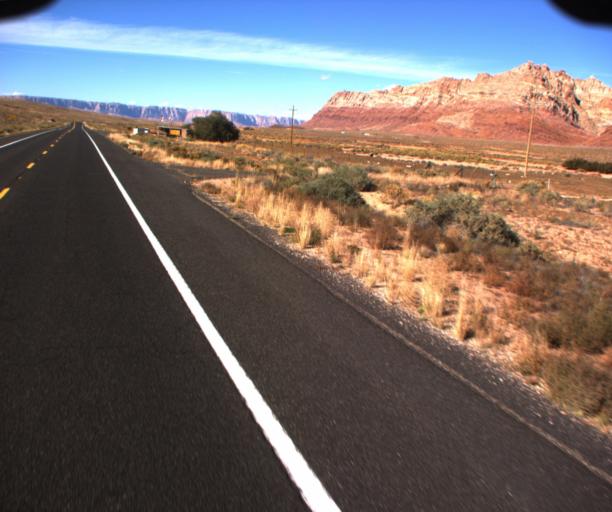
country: US
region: Arizona
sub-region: Coconino County
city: LeChee
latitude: 36.5526
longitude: -111.6279
